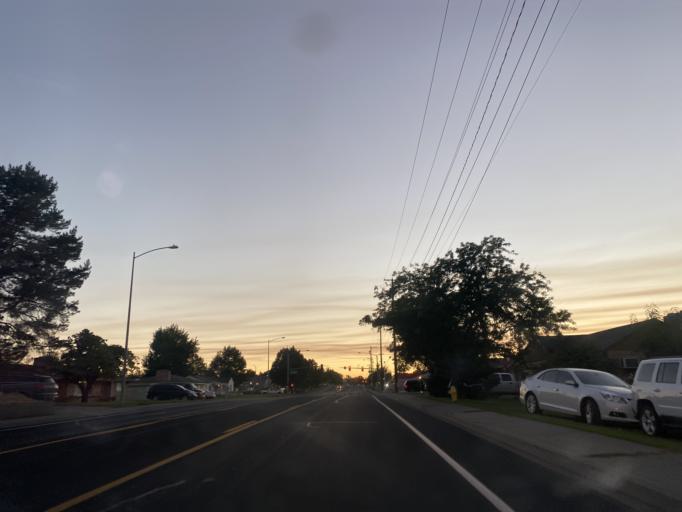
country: US
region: Washington
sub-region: Benton County
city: Kennewick
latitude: 46.1986
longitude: -119.1546
